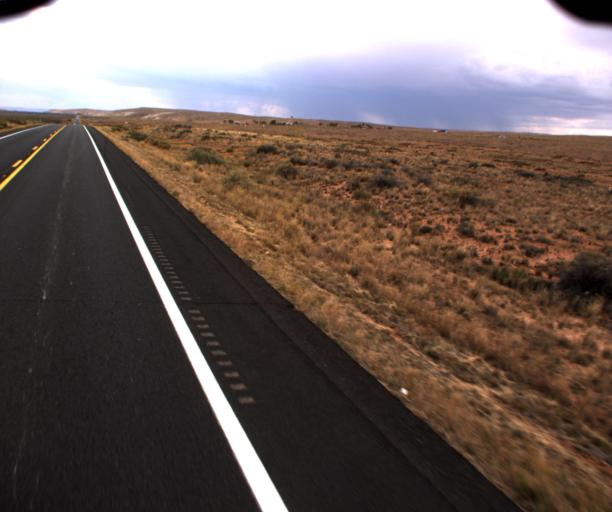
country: US
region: Arizona
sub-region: Coconino County
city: Kaibito
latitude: 36.3589
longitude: -110.9041
